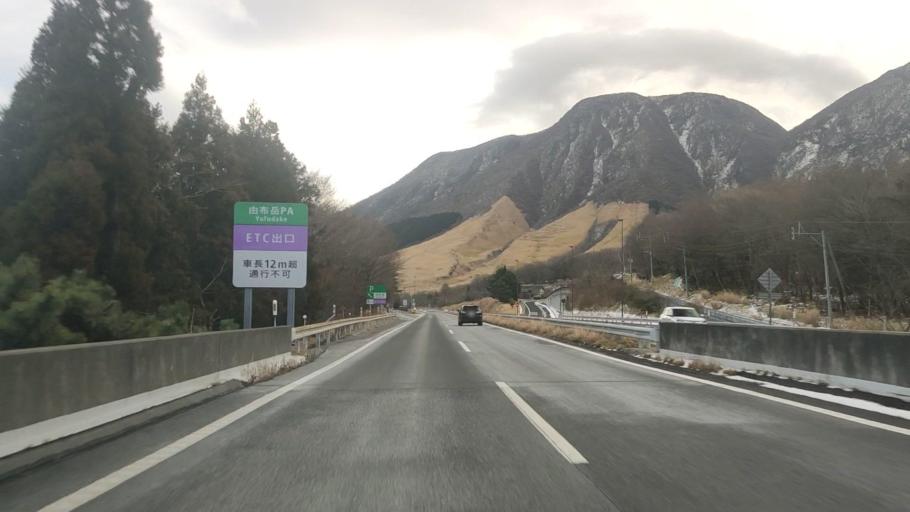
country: JP
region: Oita
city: Beppu
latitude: 33.3021
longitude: 131.3933
